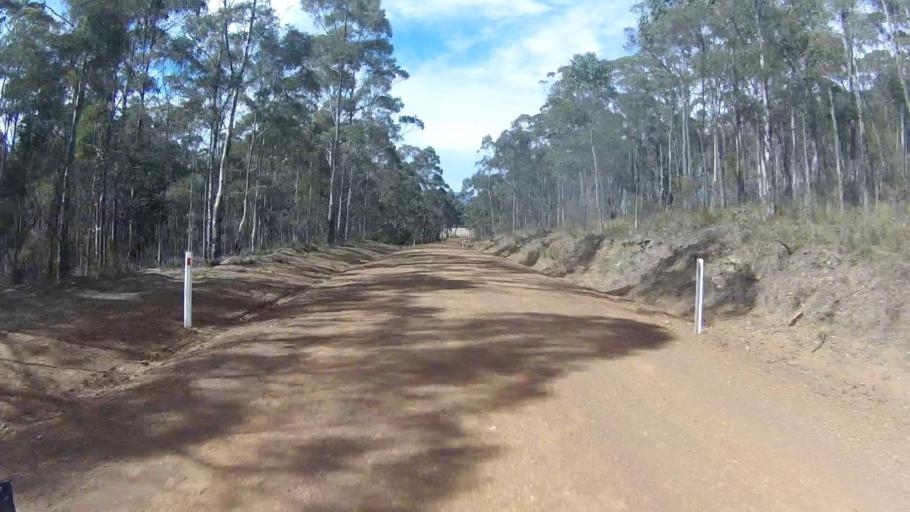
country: AU
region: Tasmania
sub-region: Sorell
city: Sorell
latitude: -42.6266
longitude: 147.9024
